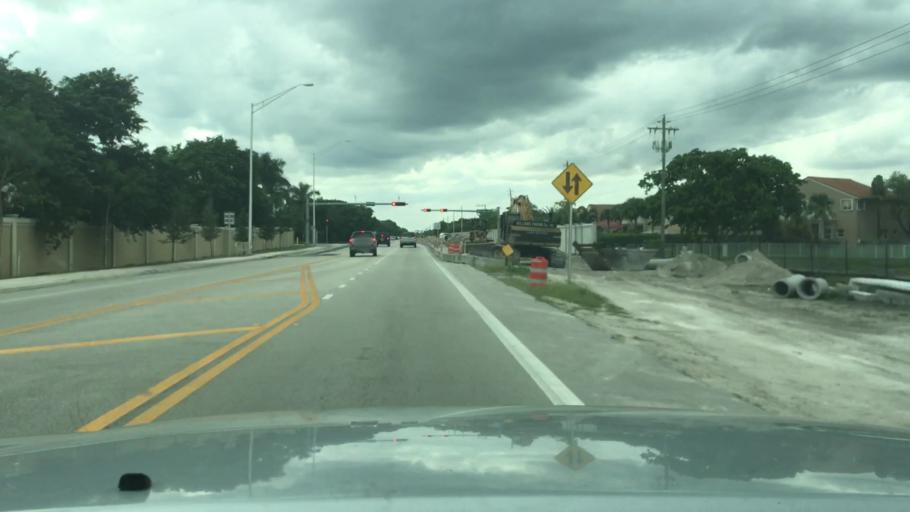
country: US
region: Florida
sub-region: Miami-Dade County
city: Country Club
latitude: 25.9931
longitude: -80.3506
